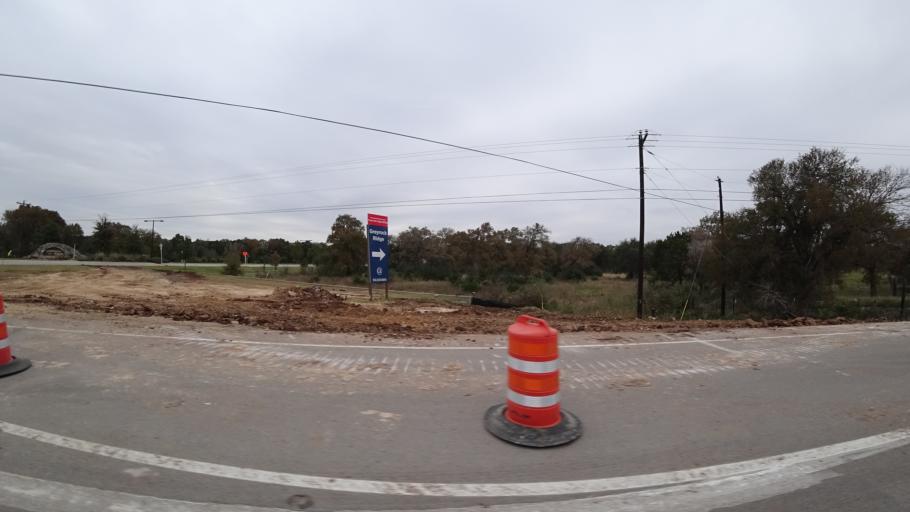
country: US
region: Texas
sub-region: Travis County
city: Shady Hollow
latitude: 30.1728
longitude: -97.8891
